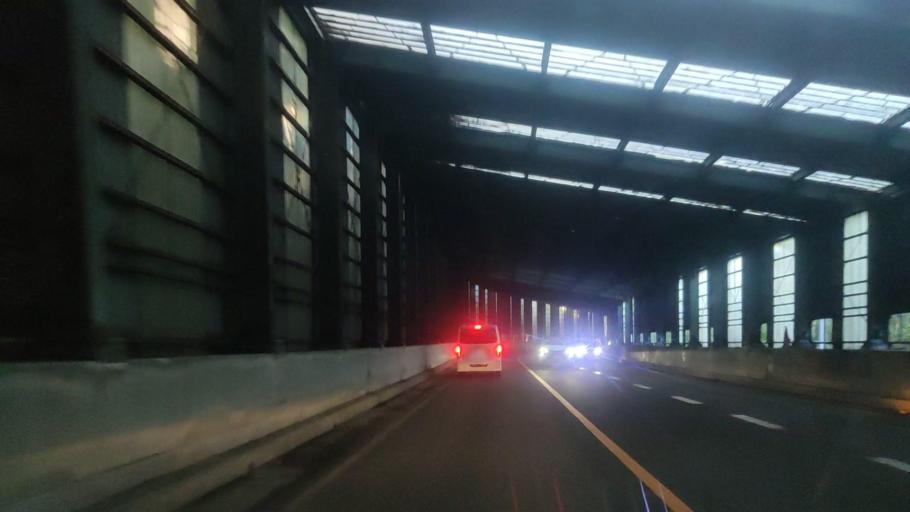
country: JP
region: Nagano
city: Kamimaruko
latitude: 36.1784
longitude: 138.2823
